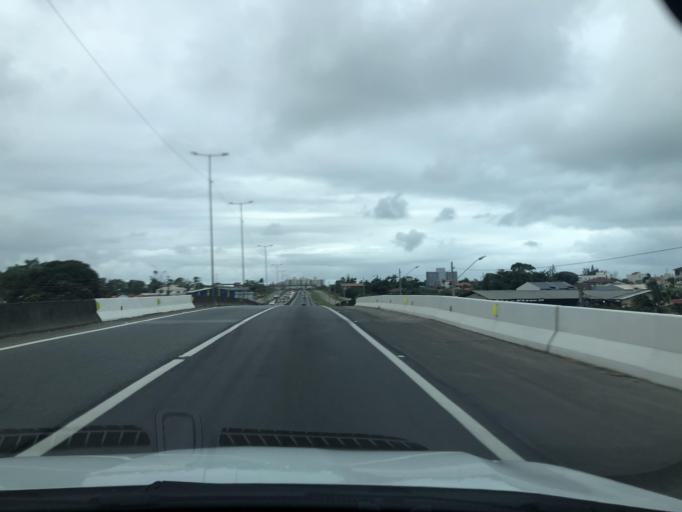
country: BR
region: Santa Catarina
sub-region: Barra Velha
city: Barra Velha
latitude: -26.6804
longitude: -48.6933
